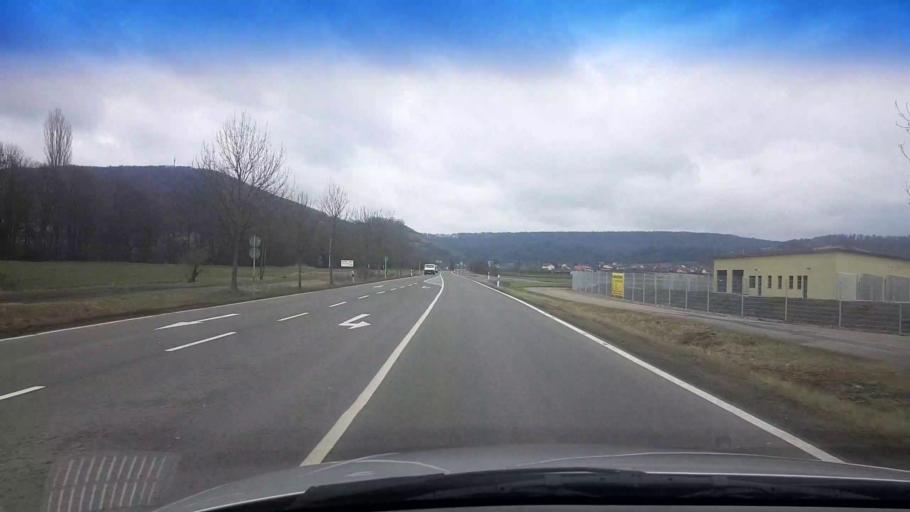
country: DE
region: Bavaria
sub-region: Regierungsbezirk Unterfranken
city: Knetzgau
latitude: 49.9777
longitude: 10.5586
